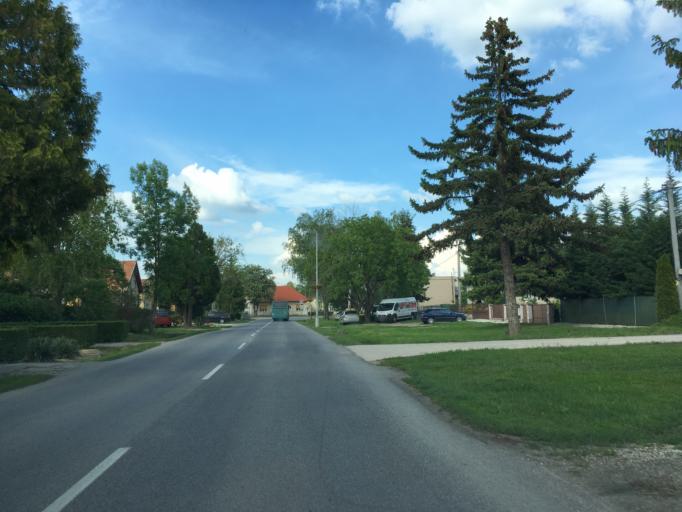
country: HU
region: Komarom-Esztergom
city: Almasfuzito
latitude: 47.7896
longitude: 18.2838
